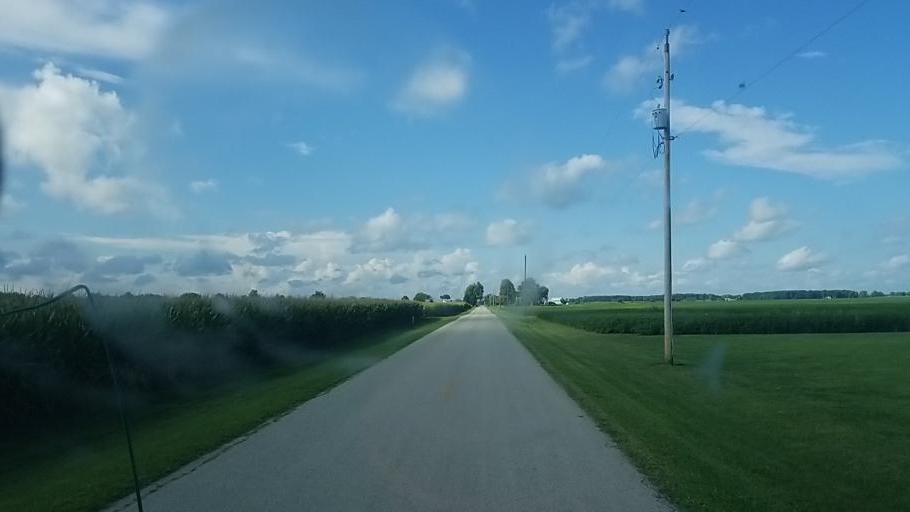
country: US
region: Ohio
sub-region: Hardin County
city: Forest
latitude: 40.7063
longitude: -83.5145
